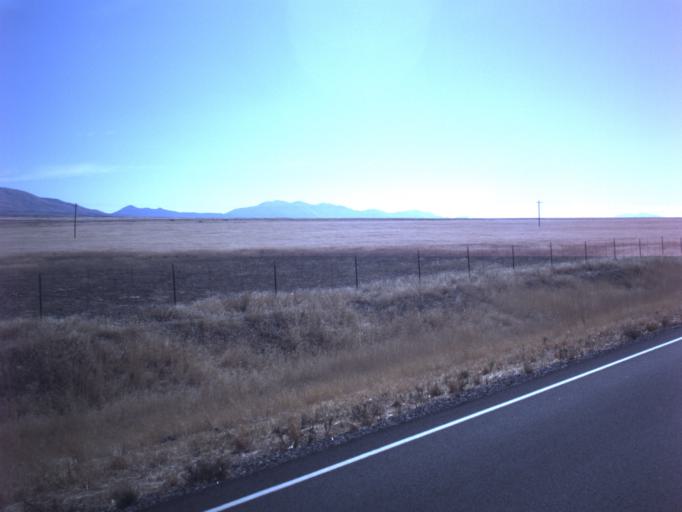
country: US
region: Utah
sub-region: Tooele County
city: Grantsville
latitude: 40.4386
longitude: -112.7487
